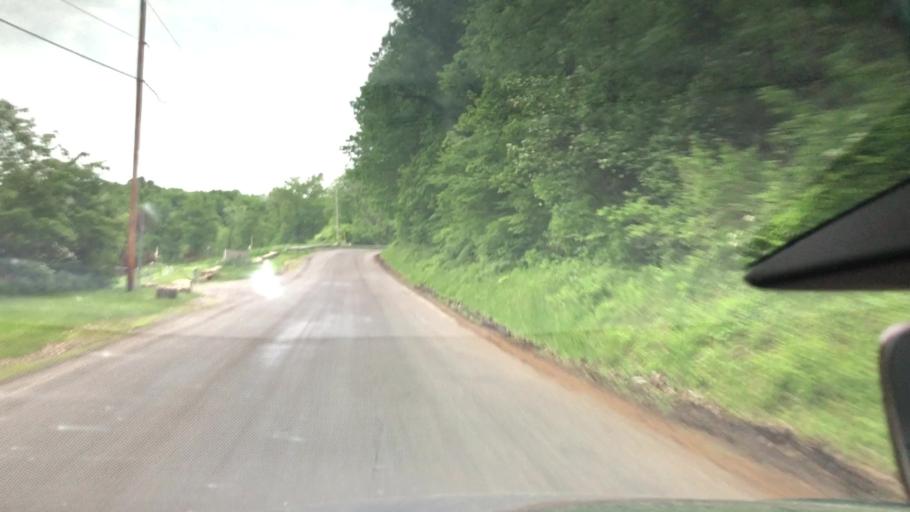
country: US
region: Pennsylvania
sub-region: Butler County
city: Saxonburg
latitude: 40.7378
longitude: -79.8553
